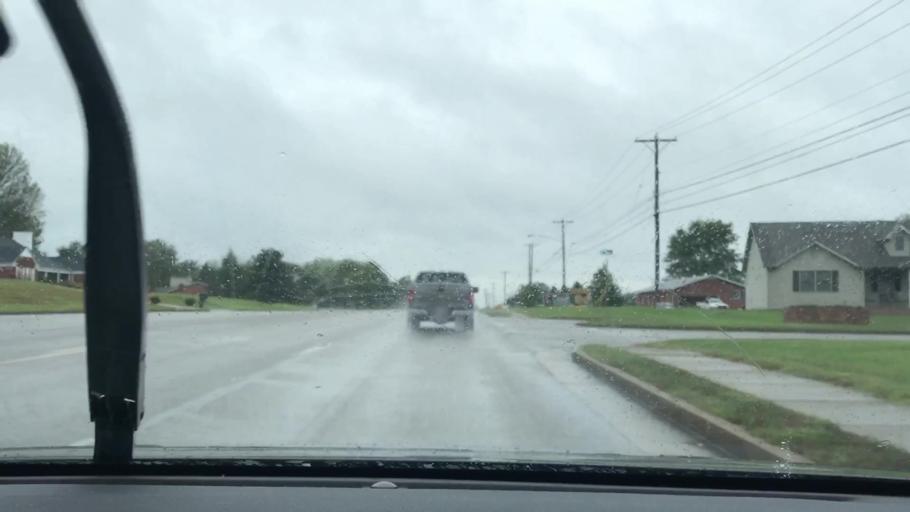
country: US
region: Kentucky
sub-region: Hopkins County
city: Madisonville
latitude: 37.3257
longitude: -87.4590
